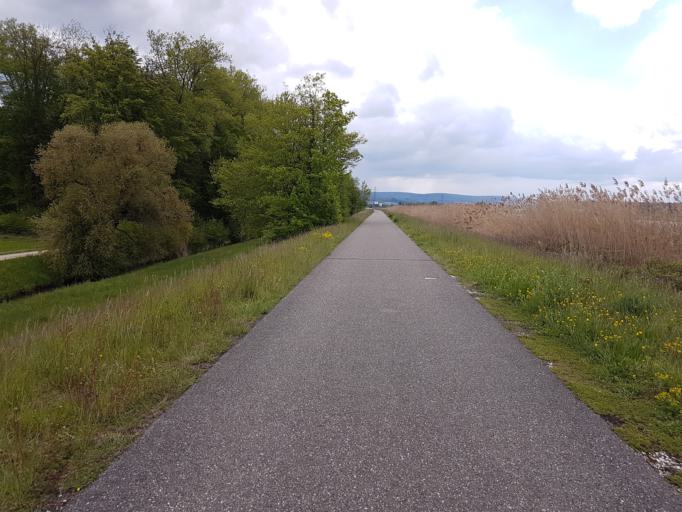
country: CH
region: Aargau
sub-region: Bezirk Zurzach
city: Koblenz
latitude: 47.5911
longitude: 8.2311
